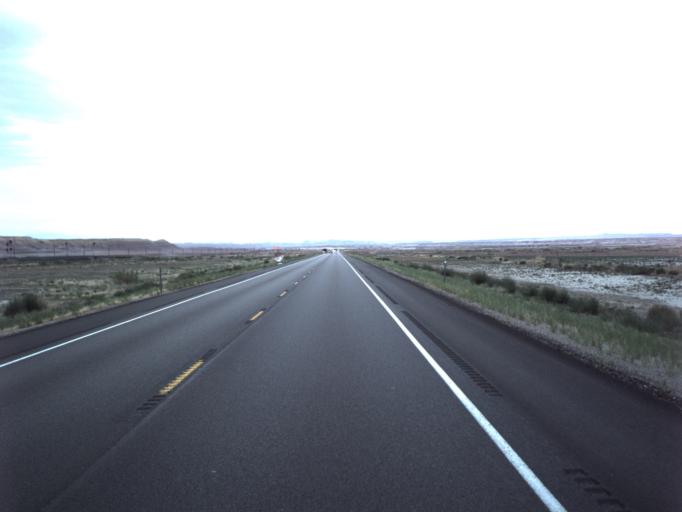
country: US
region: Utah
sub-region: Carbon County
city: East Carbon City
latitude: 39.0168
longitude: -110.2894
